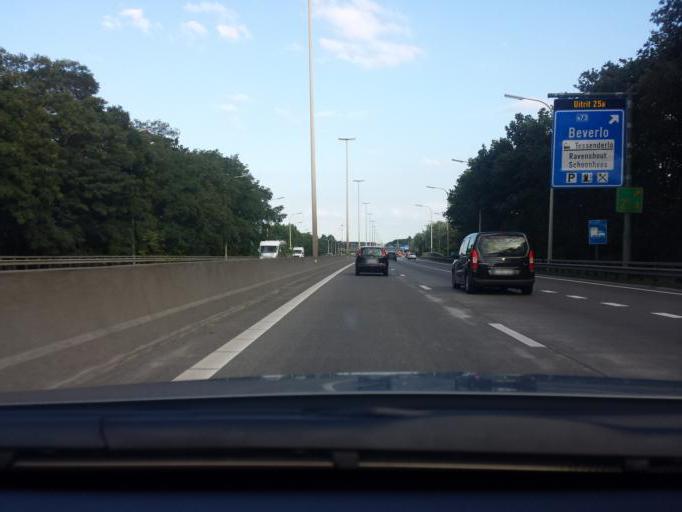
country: BE
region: Flanders
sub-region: Provincie Limburg
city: Tessenderlo
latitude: 51.0833
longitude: 5.1302
